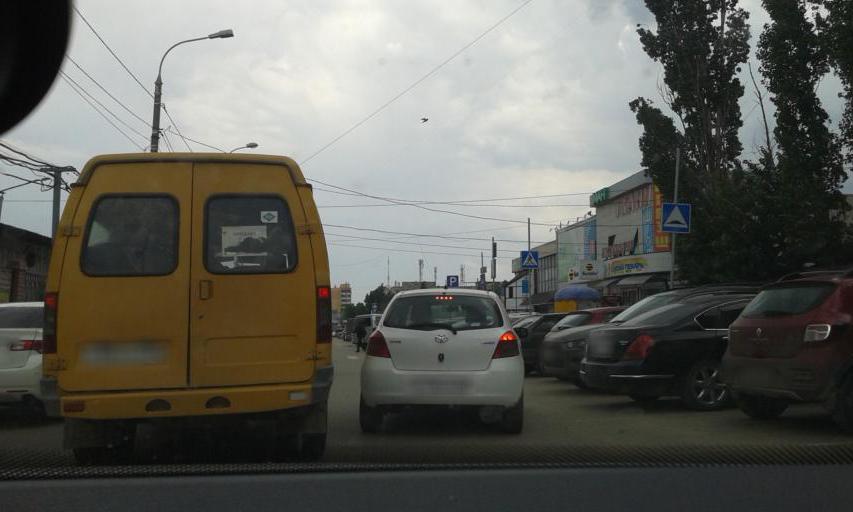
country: RU
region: Volgograd
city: Volgograd
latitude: 48.7572
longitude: 44.5017
